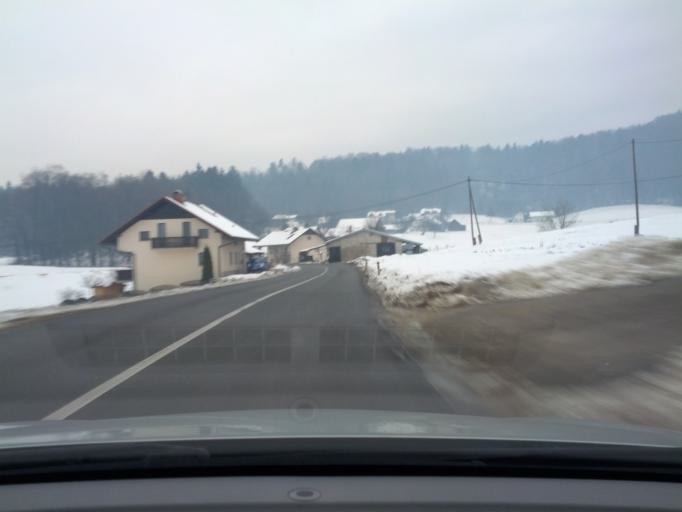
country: SI
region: Moravce
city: Moravce
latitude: 46.1393
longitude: 14.7130
